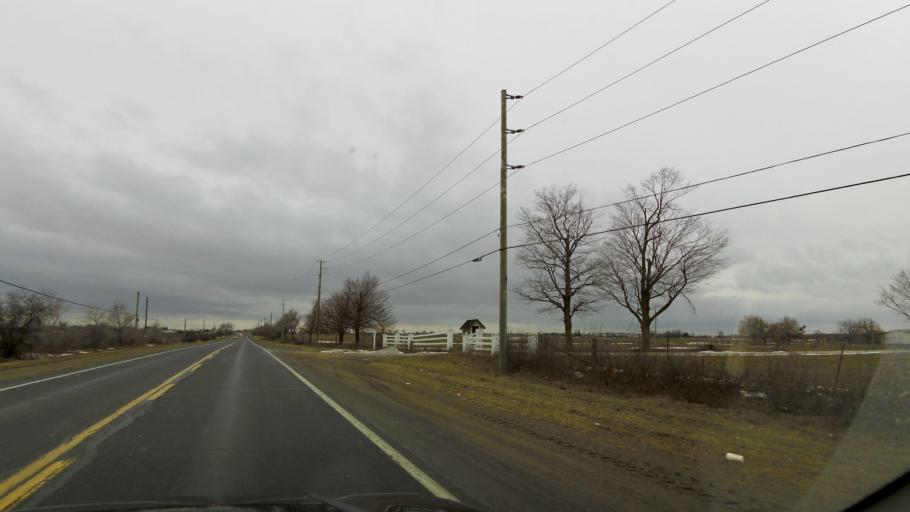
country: CA
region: Ontario
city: Brampton
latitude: 43.8387
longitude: -79.6788
